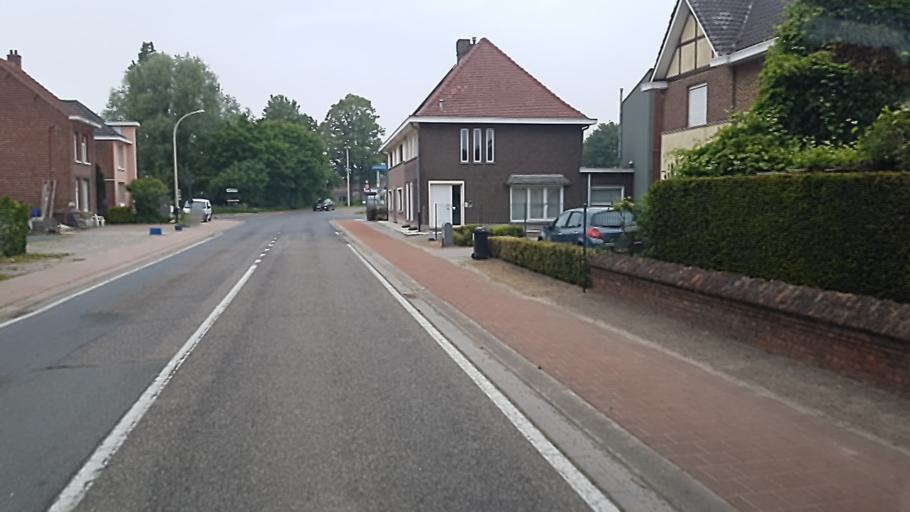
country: BE
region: Flanders
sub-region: Provincie Antwerpen
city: Brecht
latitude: 51.3372
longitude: 4.6594
